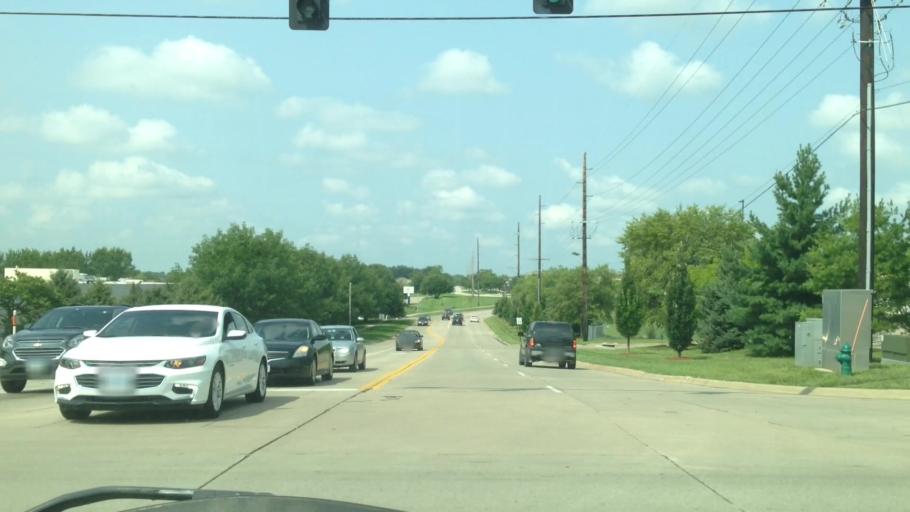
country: US
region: Iowa
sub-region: Linn County
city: Fairfax
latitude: 41.9456
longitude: -91.7161
